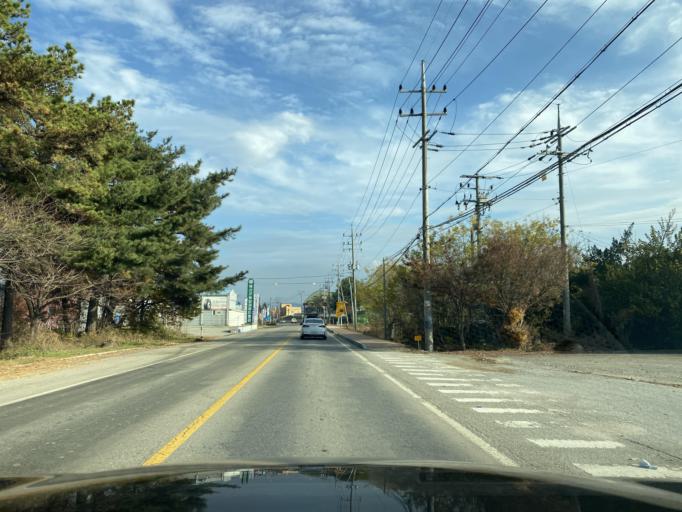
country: KR
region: Chungcheongnam-do
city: Yesan
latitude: 36.6889
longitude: 126.7918
